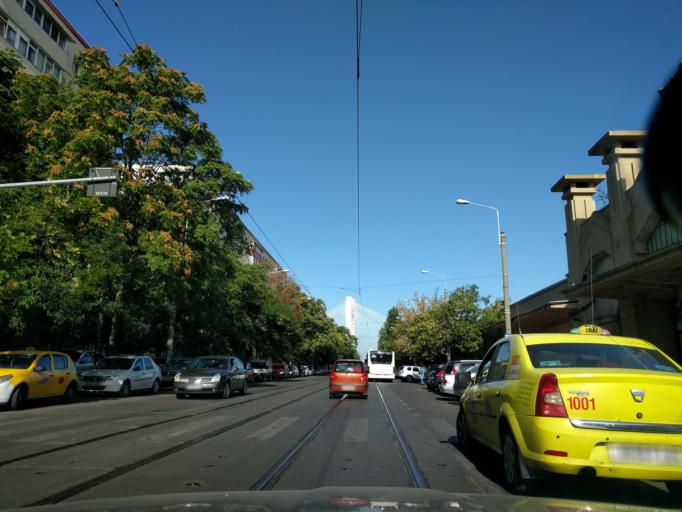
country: RO
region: Bucuresti
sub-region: Municipiul Bucuresti
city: Bucuresti
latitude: 44.4462
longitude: 26.0734
